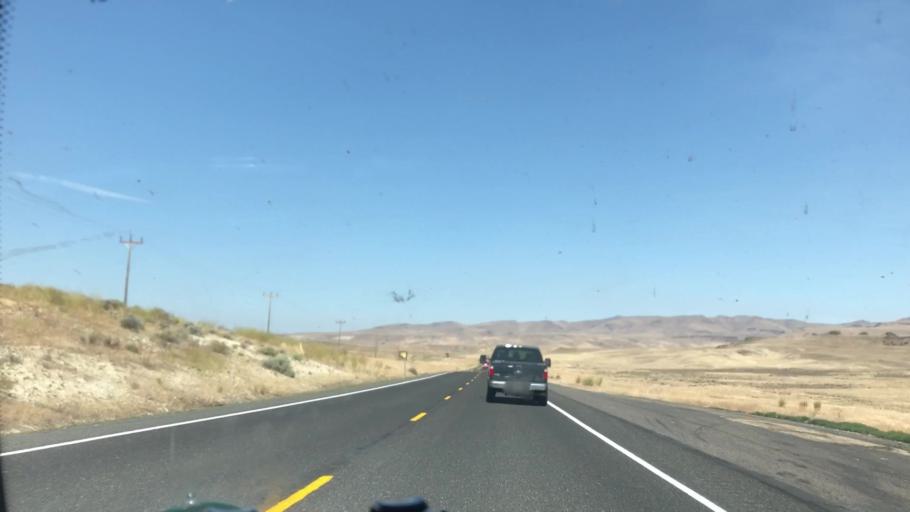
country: US
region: Idaho
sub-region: Owyhee County
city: Marsing
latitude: 43.2423
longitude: -117.0400
